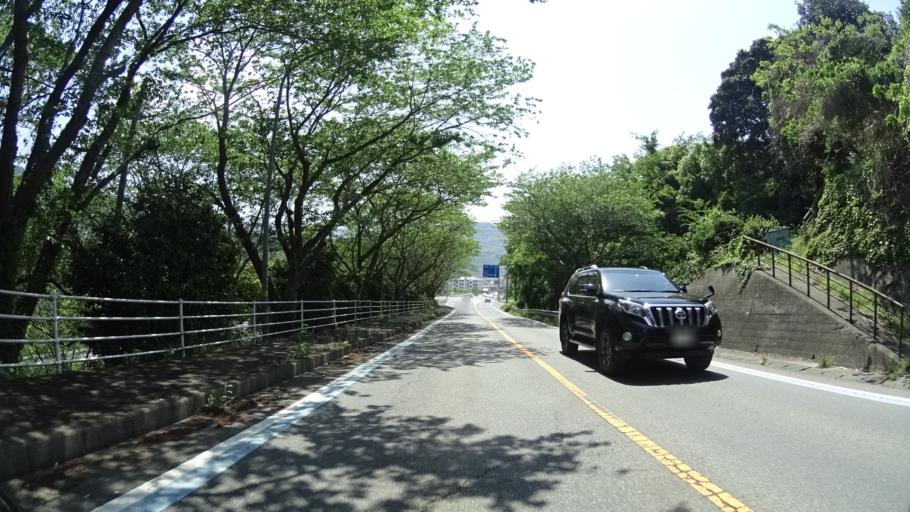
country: JP
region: Ehime
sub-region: Nishiuwa-gun
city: Ikata-cho
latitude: 33.4897
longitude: 132.3960
